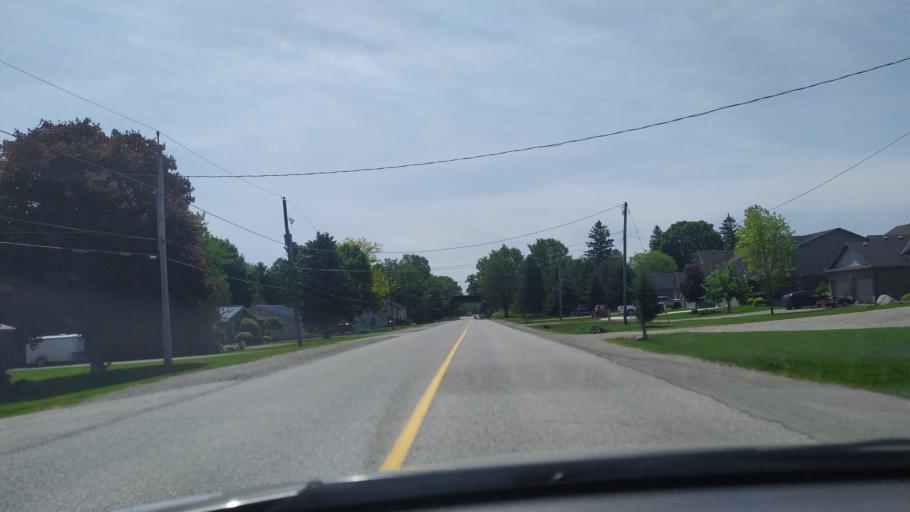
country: CA
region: Ontario
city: Dorchester
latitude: 43.0657
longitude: -81.0006
